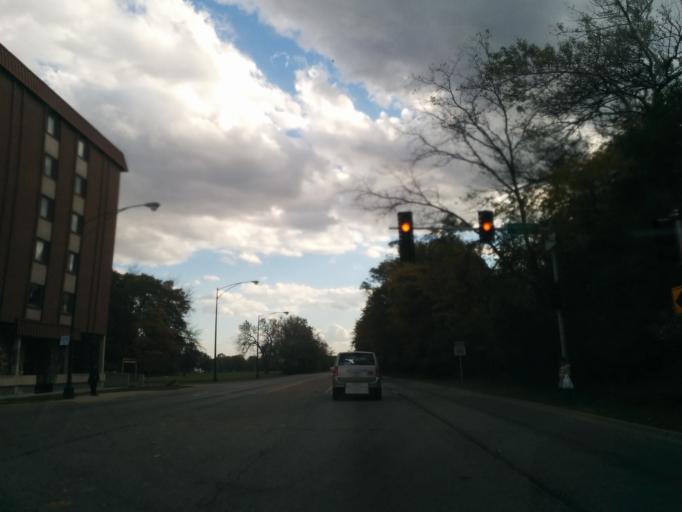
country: US
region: Illinois
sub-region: Cook County
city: River Grove
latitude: 41.9450
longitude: -87.8365
